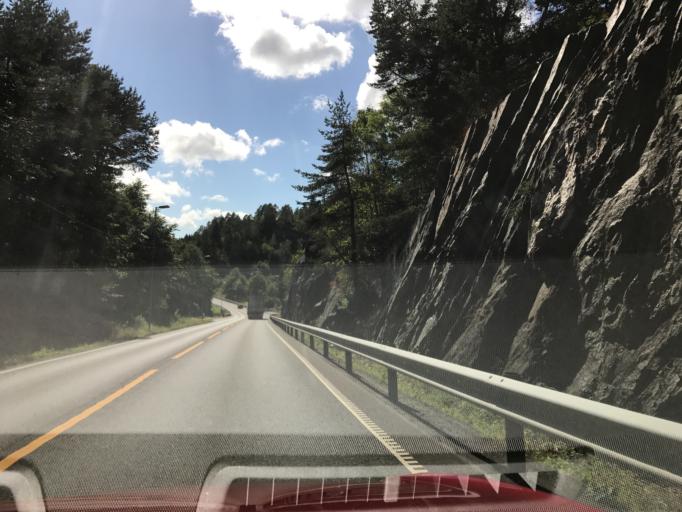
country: NO
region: Telemark
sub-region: Bamble
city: Langesund
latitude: 58.9928
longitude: 9.6377
